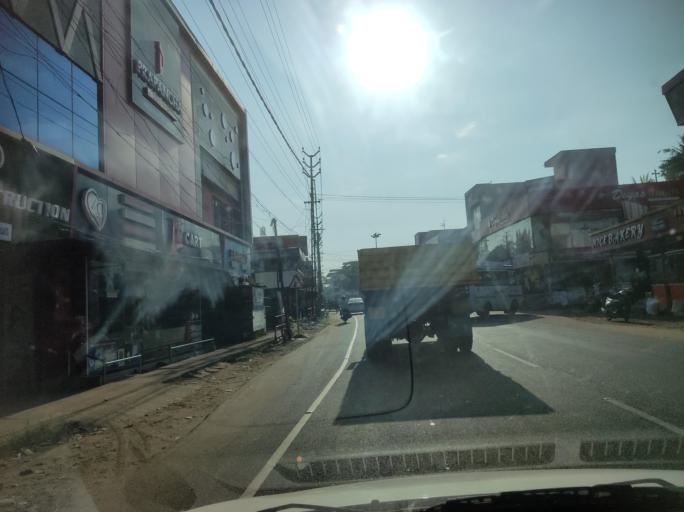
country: IN
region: Kerala
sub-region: Alappuzha
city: Kattanam
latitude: 9.1764
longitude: 76.5632
